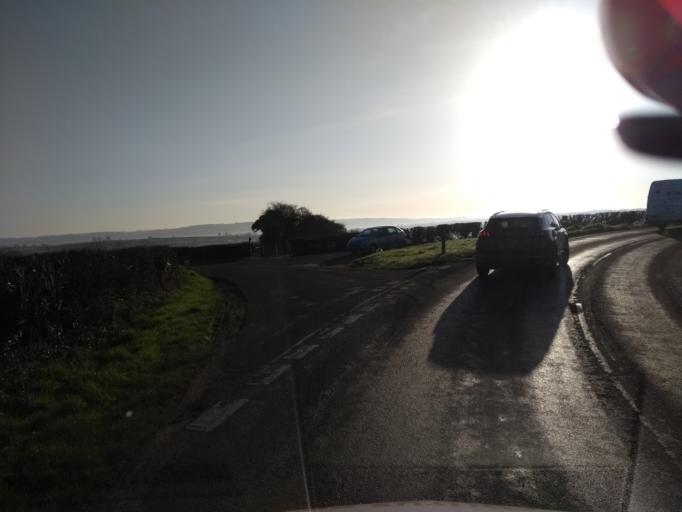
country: GB
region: England
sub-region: Somerset
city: Bruton
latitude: 51.1291
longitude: -2.4686
